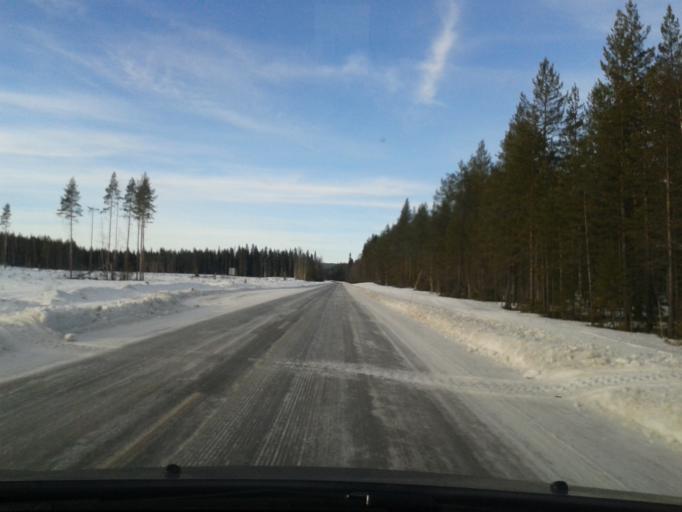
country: SE
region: Vaesternorrland
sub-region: OErnskoeldsviks Kommun
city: Bredbyn
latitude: 63.5964
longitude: 17.9156
